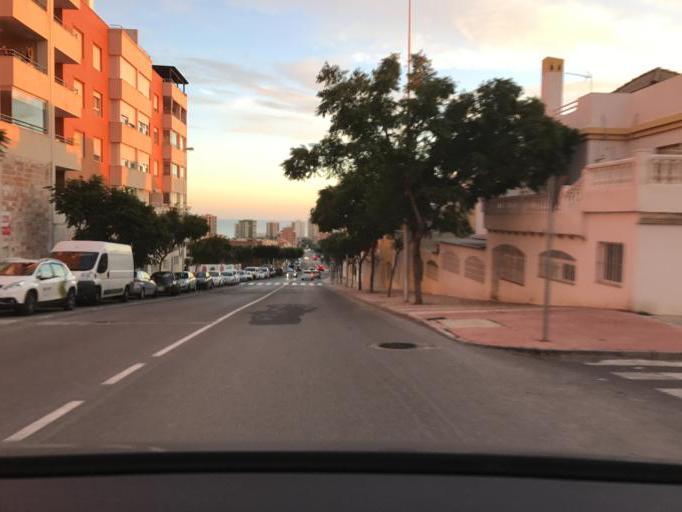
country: ES
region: Andalusia
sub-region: Provincia de Almeria
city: Aguadulce
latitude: 36.8190
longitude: -2.5818
